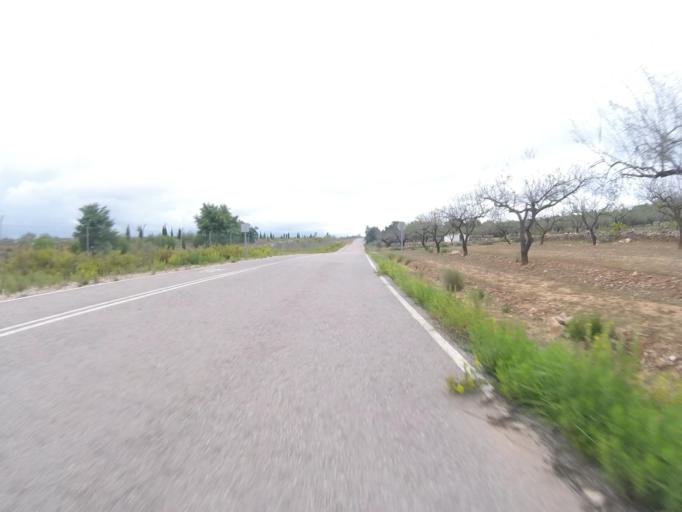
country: ES
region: Valencia
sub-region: Provincia de Castello
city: Cabanes
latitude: 40.1674
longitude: 0.0421
